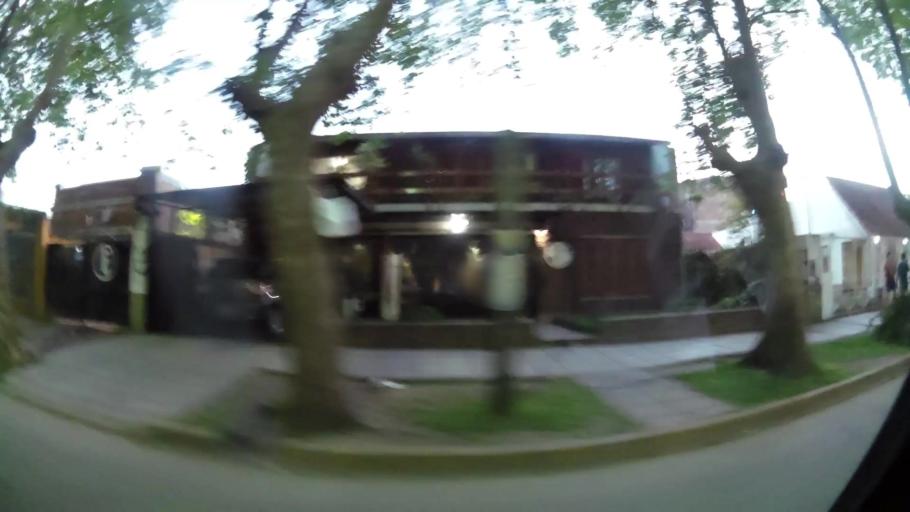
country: AR
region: Buenos Aires
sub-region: Partido de Quilmes
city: Quilmes
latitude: -34.8092
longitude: -58.2792
